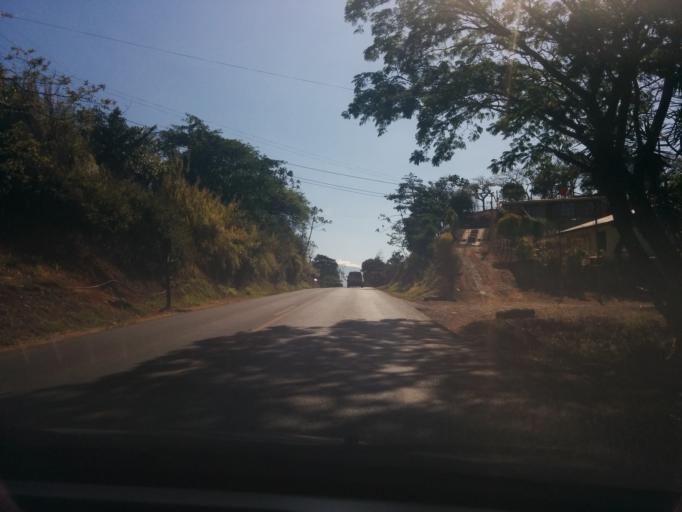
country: CR
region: Alajuela
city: San Rafael
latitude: 10.0717
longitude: -84.4863
